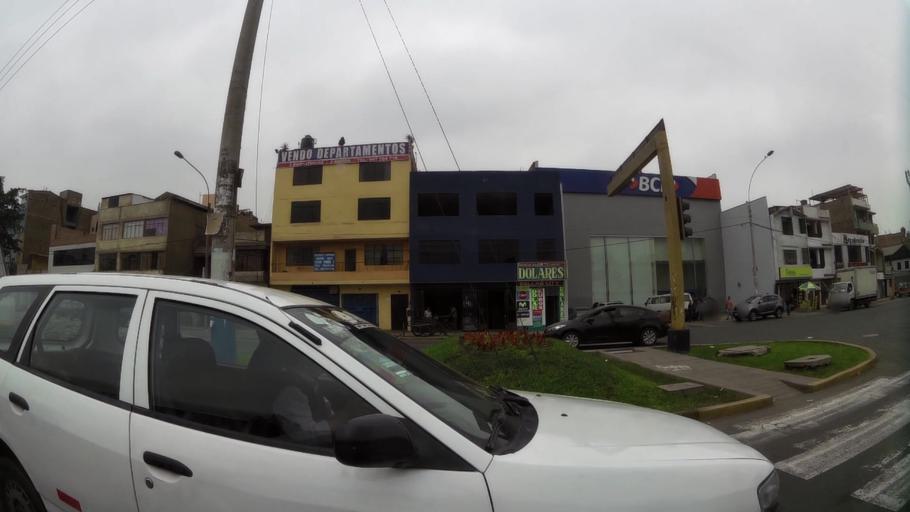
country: PE
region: Lima
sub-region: Lima
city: Independencia
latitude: -11.9389
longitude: -77.0772
